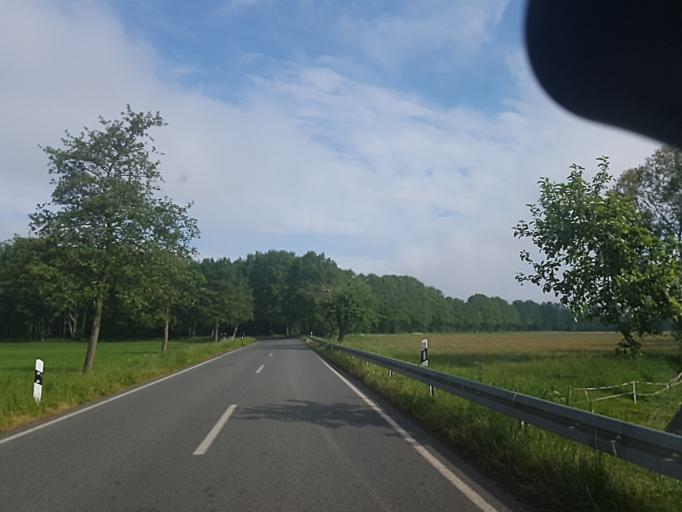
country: DE
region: Saxony-Anhalt
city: Rodleben
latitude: 52.0146
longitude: 12.2316
